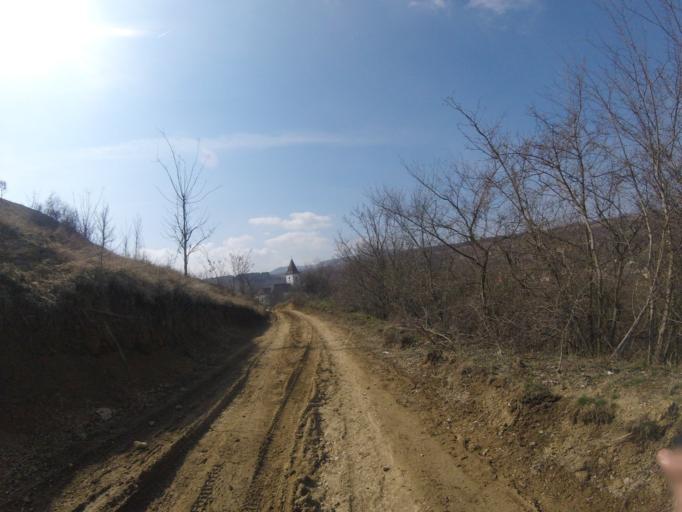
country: HU
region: Komarom-Esztergom
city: Nyergesujfalu
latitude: 47.7501
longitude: 18.5536
